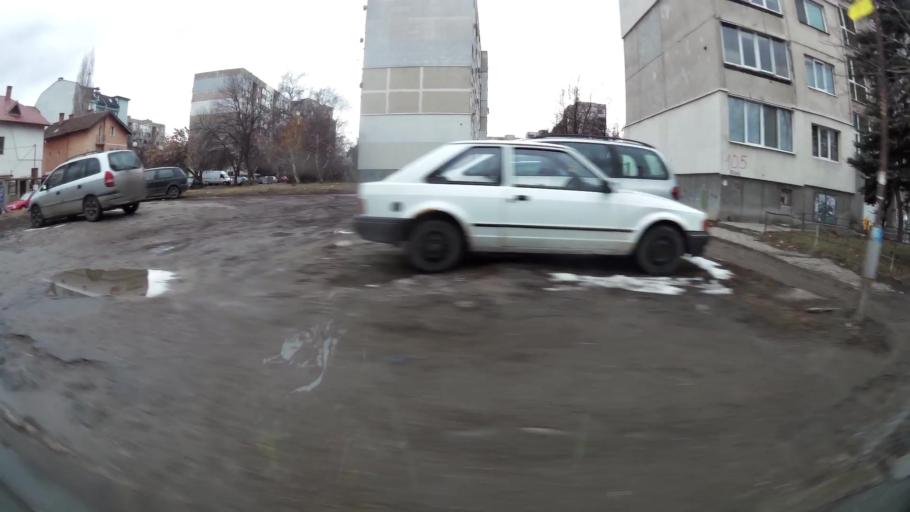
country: BG
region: Sofia-Capital
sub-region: Stolichna Obshtina
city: Sofia
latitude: 42.7274
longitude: 23.2938
